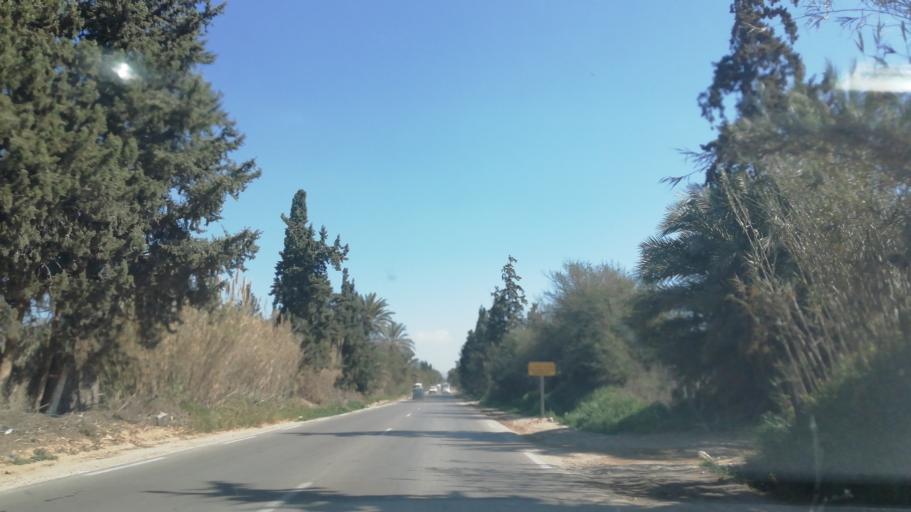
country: DZ
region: Mascara
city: Sig
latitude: 35.5799
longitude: 0.0171
